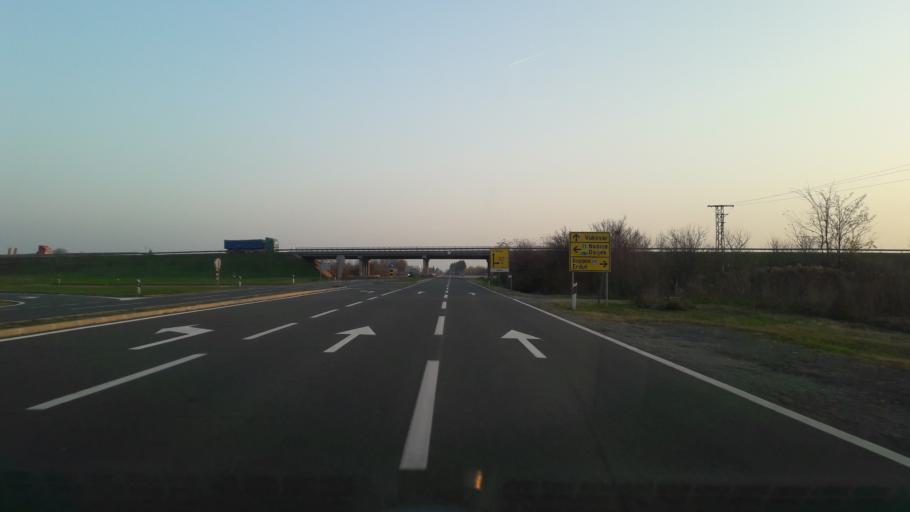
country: HR
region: Osjecko-Baranjska
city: Tenja
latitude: 45.5265
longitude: 18.7764
